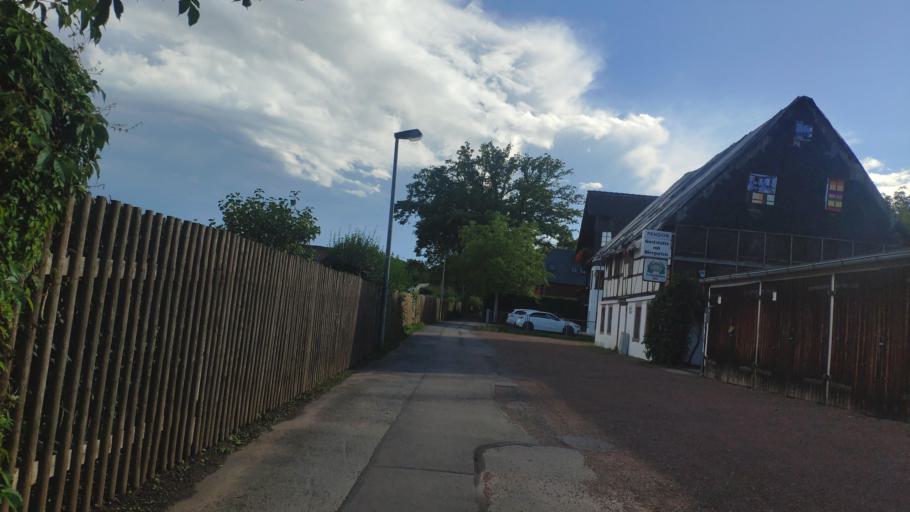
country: DE
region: Saxony
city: Neukirchen
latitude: 50.8059
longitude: 12.8991
